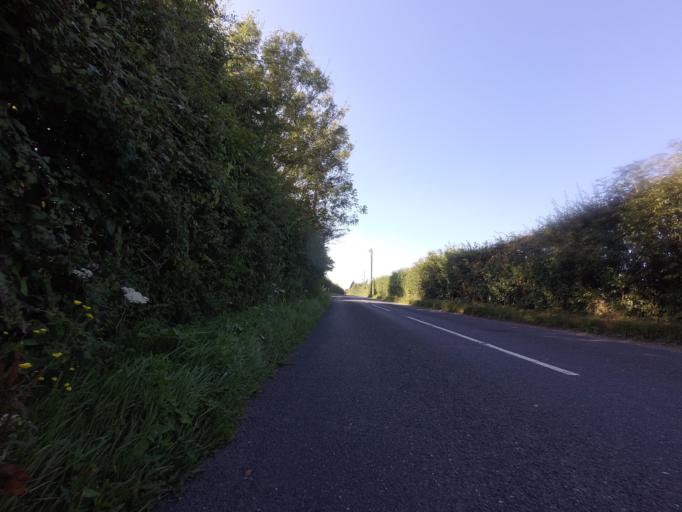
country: GB
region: England
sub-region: Kent
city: Tenterden
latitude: 51.0508
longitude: 0.6940
